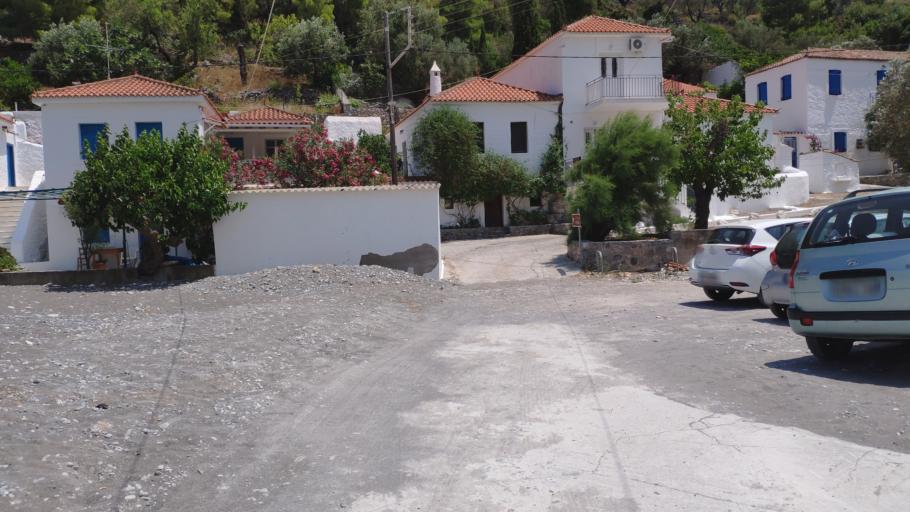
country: GR
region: Peloponnese
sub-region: Nomos Lakonias
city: Sykea
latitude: 36.9707
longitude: 22.9947
